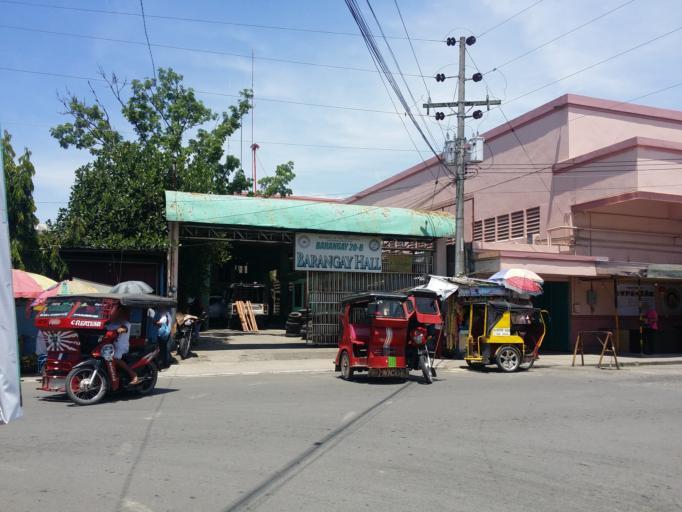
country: PH
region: Davao
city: Davao
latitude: 7.0870
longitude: 125.6131
